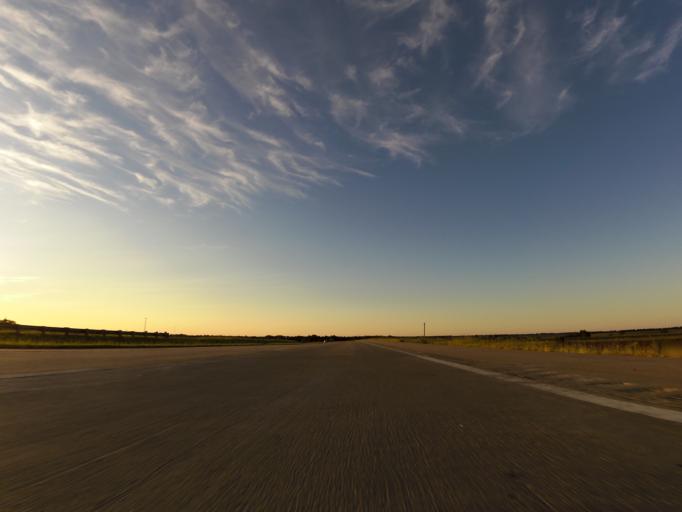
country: US
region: Kansas
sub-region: Reno County
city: South Hutchinson
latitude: 37.9402
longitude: -97.8809
